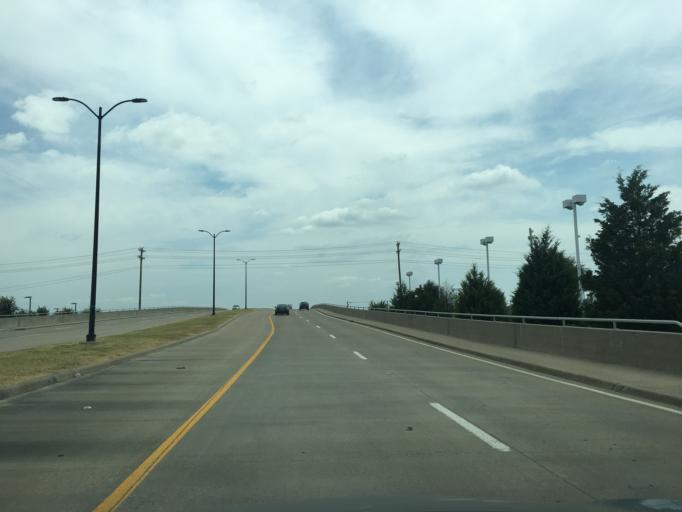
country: US
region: Texas
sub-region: Collin County
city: Frisco
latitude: 33.1020
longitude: -96.7988
